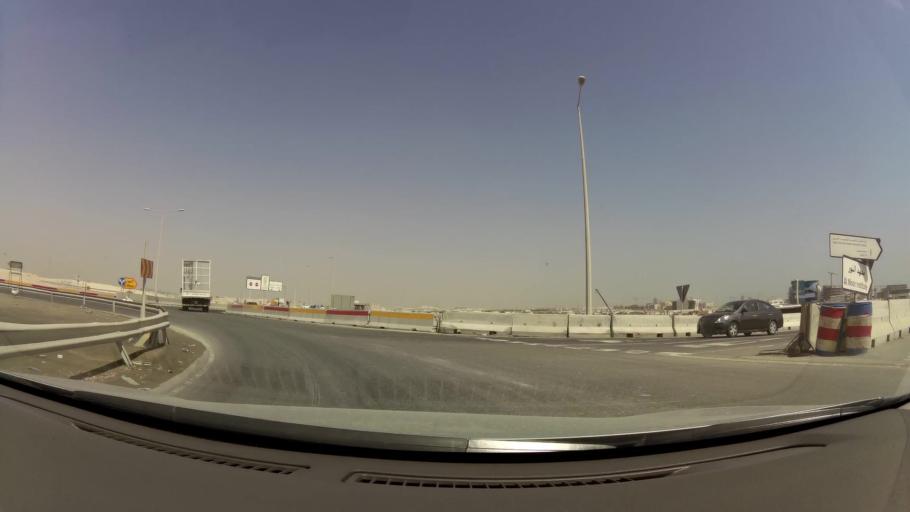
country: QA
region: Baladiyat Umm Salal
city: Umm Salal Muhammad
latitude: 25.3946
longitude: 51.5001
